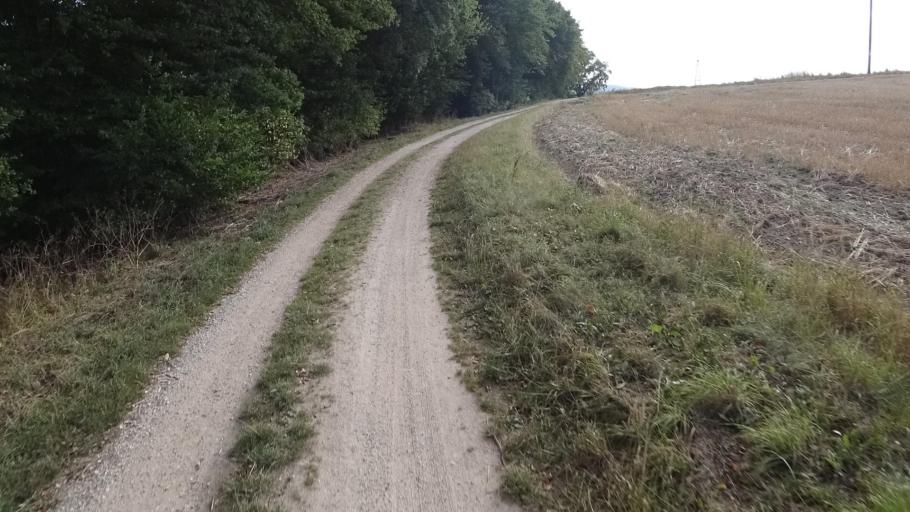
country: DE
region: Rheinland-Pfalz
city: Dichtelbach
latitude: 50.0027
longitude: 7.6873
